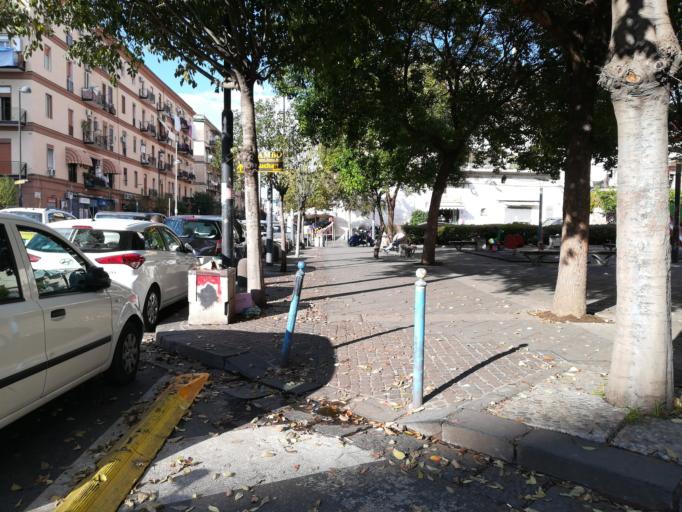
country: IT
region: Campania
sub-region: Provincia di Napoli
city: Napoli
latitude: 40.8602
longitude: 14.2706
